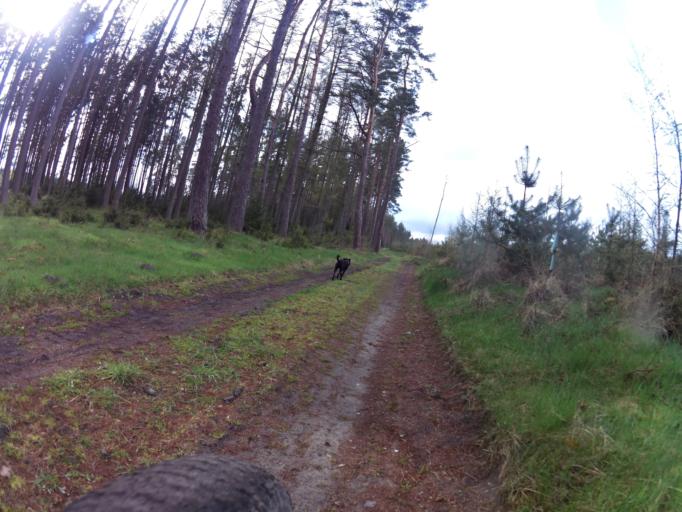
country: PL
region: Pomeranian Voivodeship
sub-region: Powiat slupski
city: Kepice
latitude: 54.2970
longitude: 16.8340
